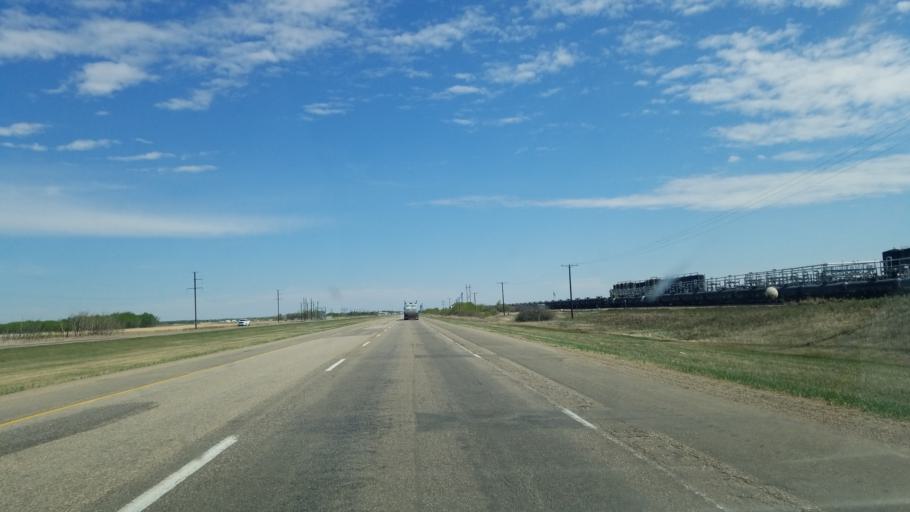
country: CA
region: Saskatchewan
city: Lloydminster
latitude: 53.1417
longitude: -109.6594
